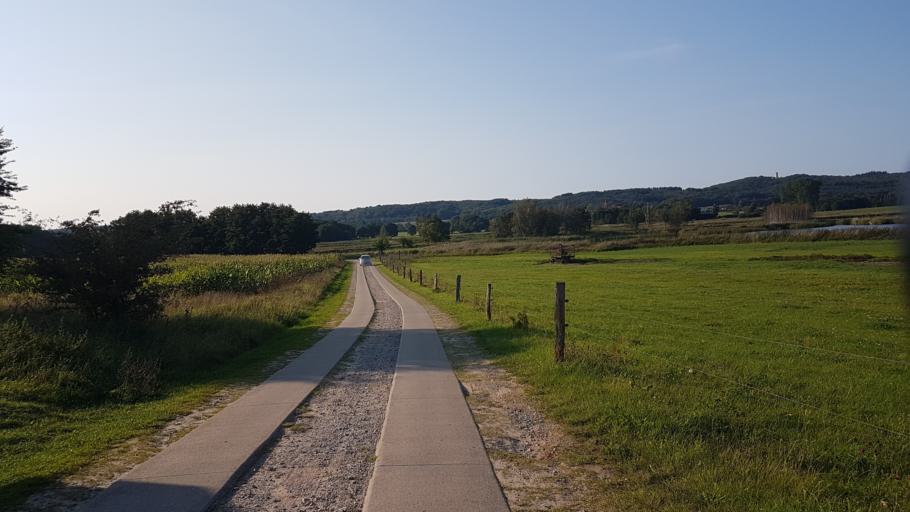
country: DE
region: Mecklenburg-Vorpommern
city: Ostseebad Sellin
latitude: 54.3568
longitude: 13.6452
